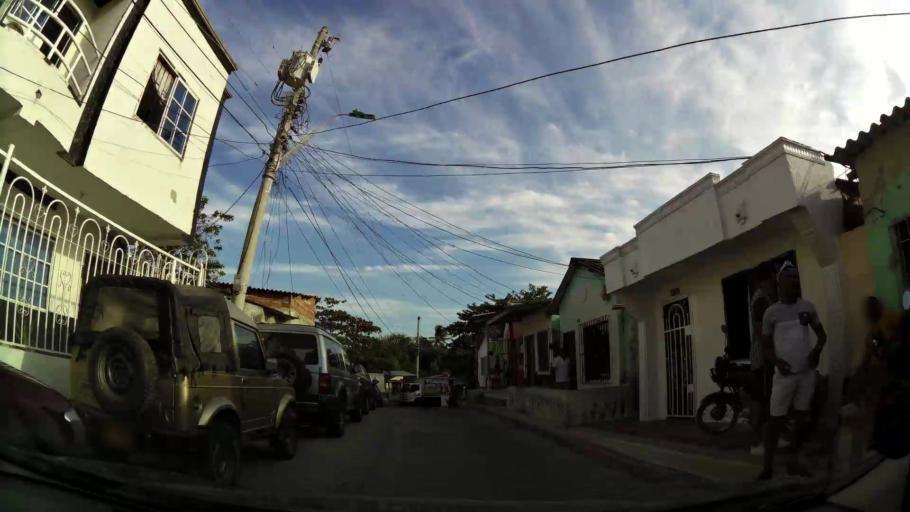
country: CO
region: Atlantico
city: Barranquilla
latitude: 10.9453
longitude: -74.8201
